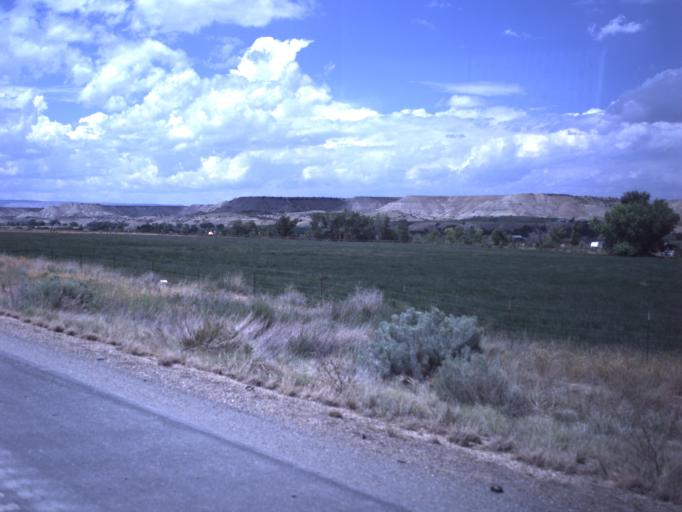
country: US
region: Utah
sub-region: Duchesne County
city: Duchesne
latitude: 40.1696
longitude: -110.3195
